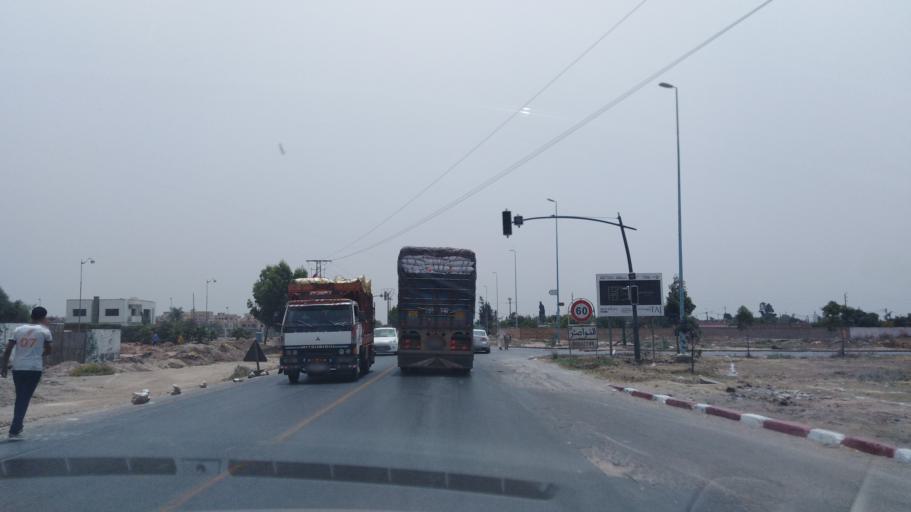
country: MA
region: Grand Casablanca
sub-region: Mediouna
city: Mediouna
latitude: 33.3883
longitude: -7.5366
